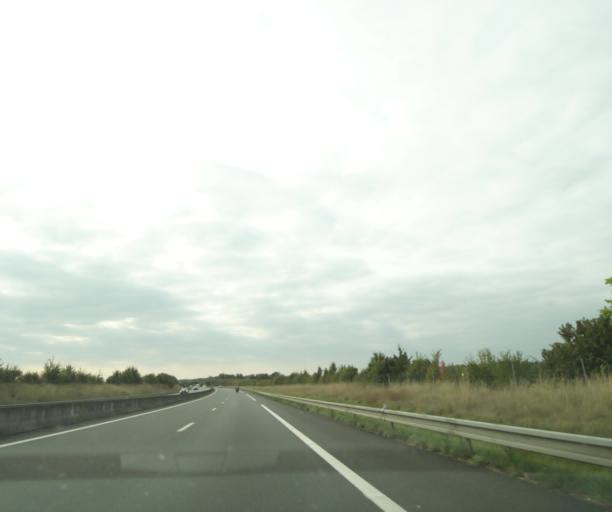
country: FR
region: Pays de la Loire
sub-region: Departement de la Sarthe
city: Chateau-du-Loir
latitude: 47.6591
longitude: 0.4360
